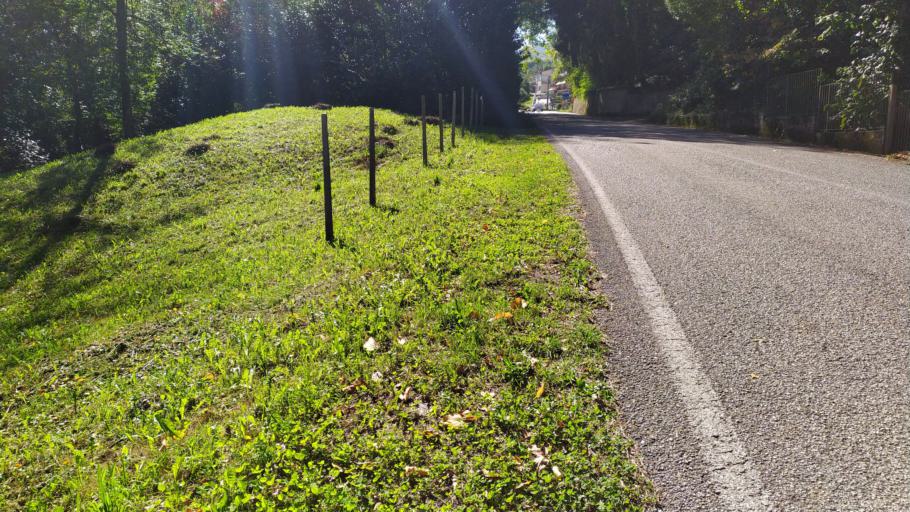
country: IT
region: Veneto
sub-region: Provincia di Vicenza
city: San Vito di Leguzzano
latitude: 45.6804
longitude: 11.3730
